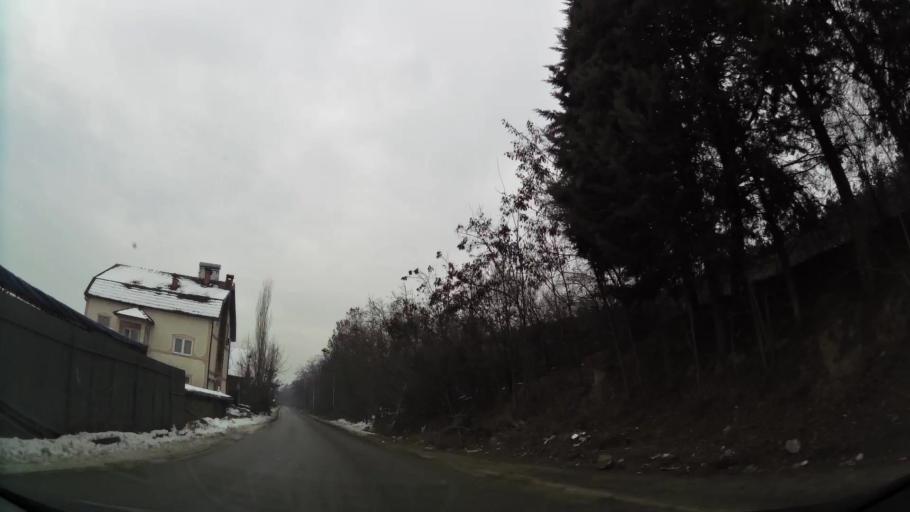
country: MK
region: Saraj
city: Saraj
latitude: 42.0104
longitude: 21.3328
